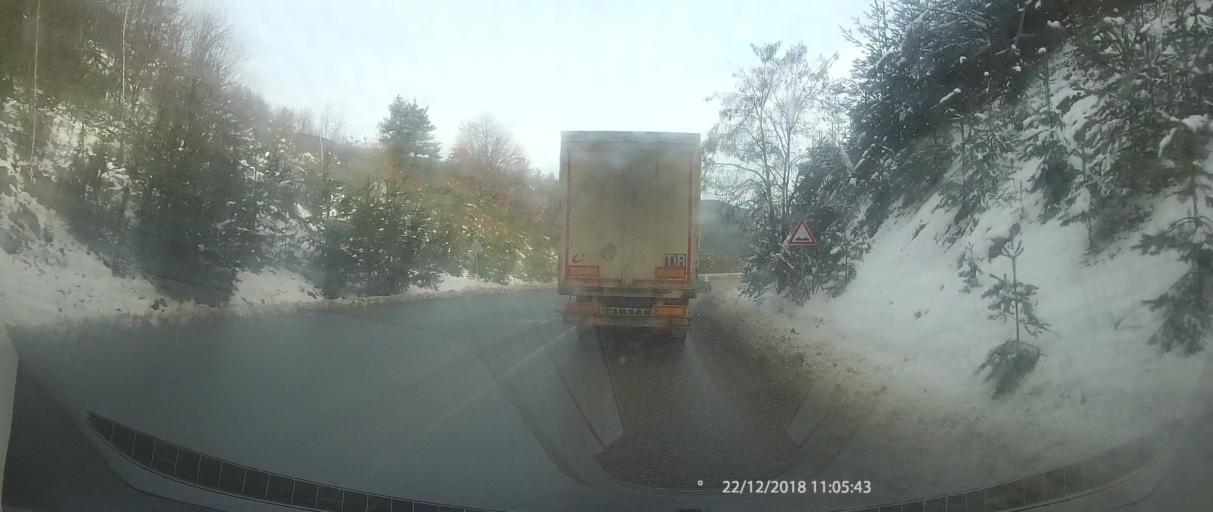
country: BG
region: Kyustendil
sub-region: Obshtina Kyustendil
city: Kyustendil
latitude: 42.2657
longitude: 22.5781
